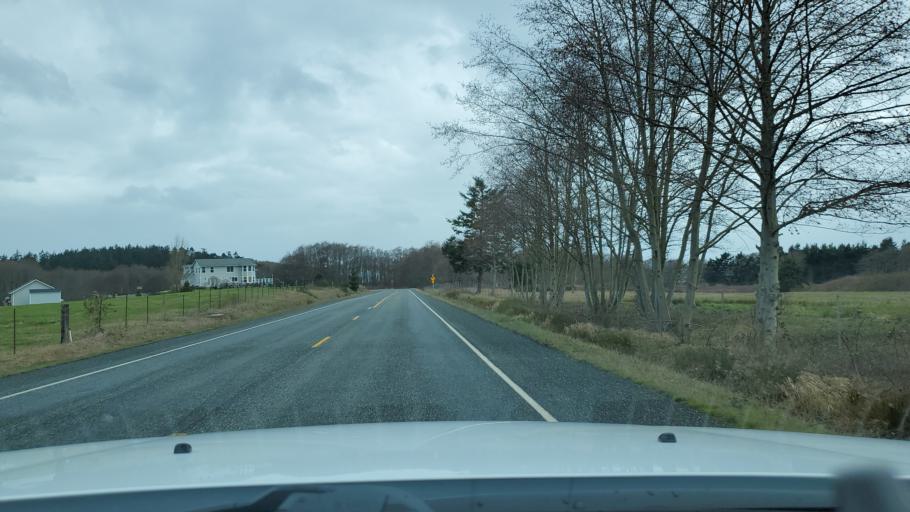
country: US
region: Washington
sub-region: Island County
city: Ault Field
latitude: 48.3114
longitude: -122.6976
